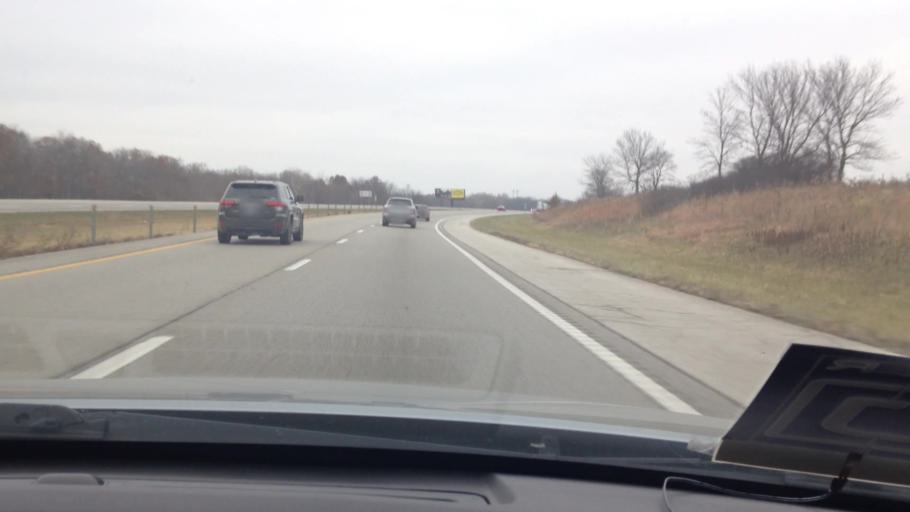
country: US
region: Missouri
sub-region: Cass County
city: Peculiar
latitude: 38.7611
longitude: -94.4874
